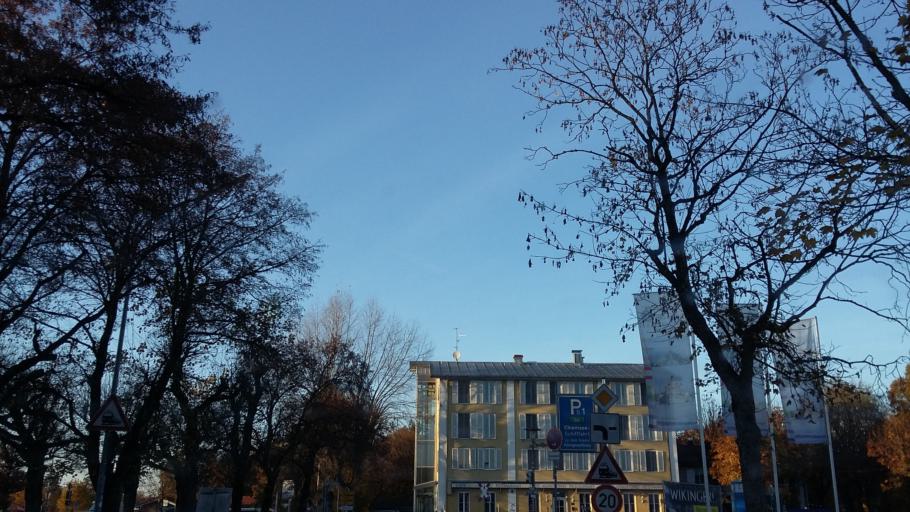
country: DE
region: Bavaria
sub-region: Upper Bavaria
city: Prien am Chiemsee
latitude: 47.8600
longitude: 12.3642
